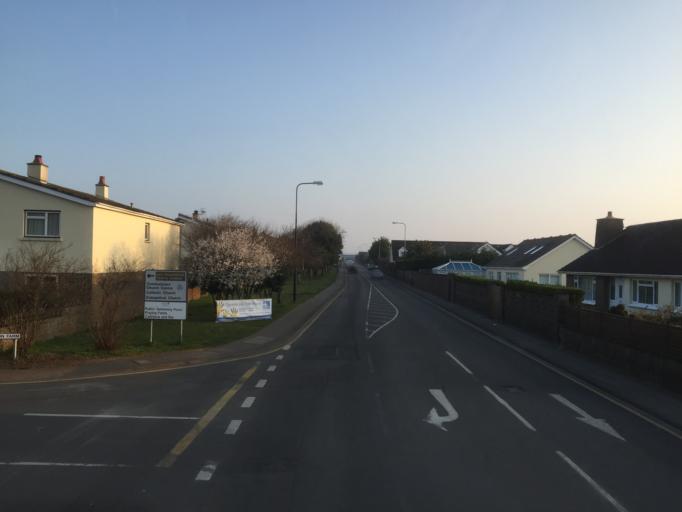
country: JE
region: St Helier
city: Saint Helier
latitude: 49.1950
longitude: -2.1987
